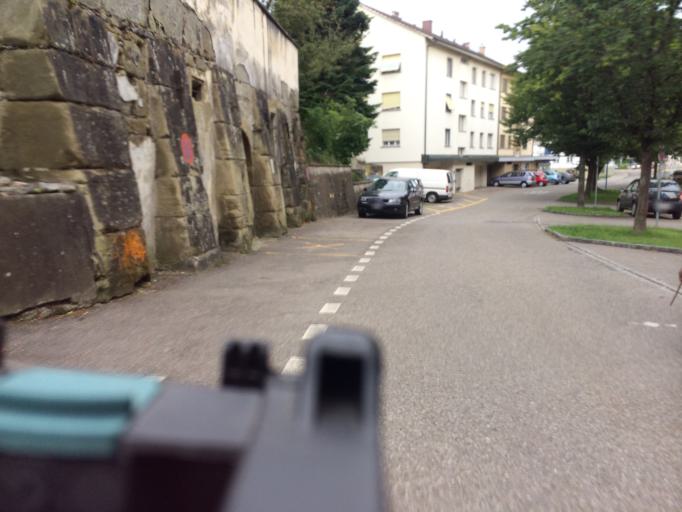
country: CH
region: Bern
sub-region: Bern-Mittelland District
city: Bolligen
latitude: 46.9731
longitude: 7.4775
